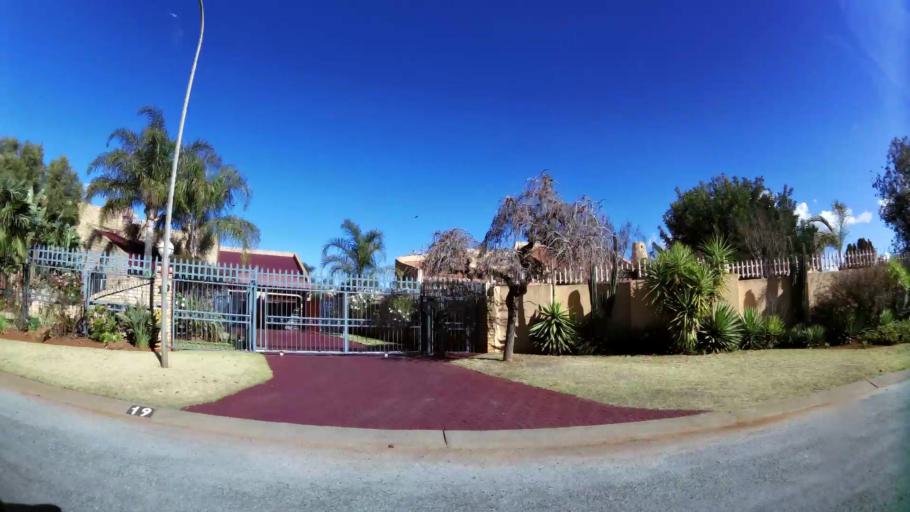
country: ZA
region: Gauteng
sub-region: West Rand District Municipality
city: Carletonville
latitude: -26.3661
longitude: 27.3681
